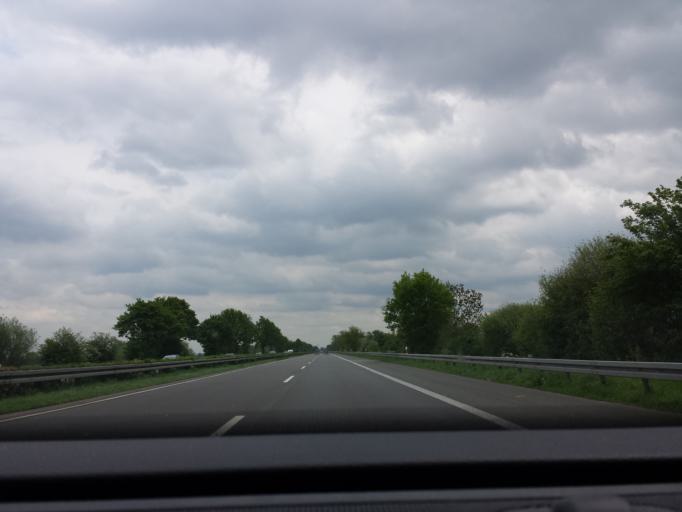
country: NL
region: Gelderland
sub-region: Oude IJsselstreek
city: Gendringen
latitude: 51.8384
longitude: 6.3530
